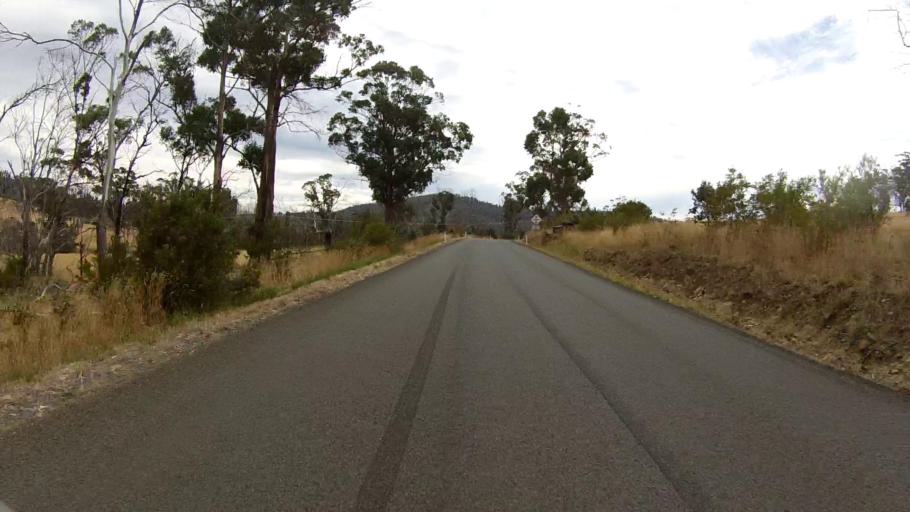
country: AU
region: Tasmania
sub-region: Sorell
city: Sorell
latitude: -42.8945
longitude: 147.7791
